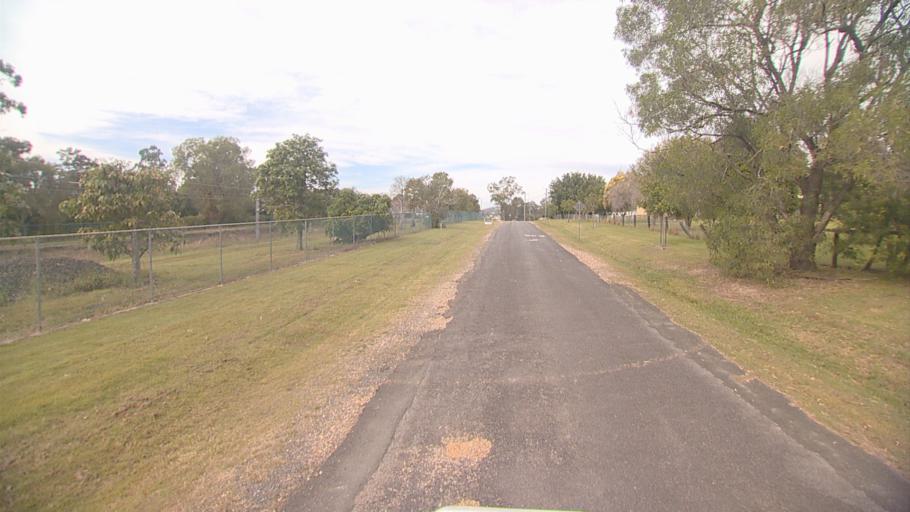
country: AU
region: Queensland
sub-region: Logan
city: Beenleigh
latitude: -27.7039
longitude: 153.1810
